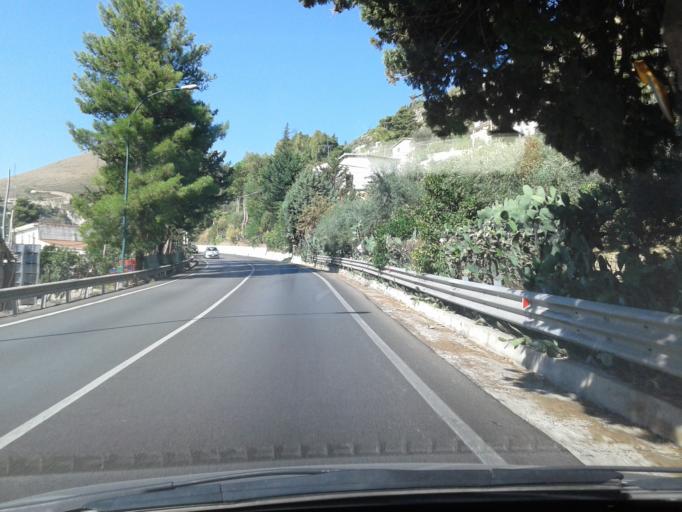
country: IT
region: Sicily
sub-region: Palermo
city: Cannizzaro-Favara
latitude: 38.0716
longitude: 13.2714
